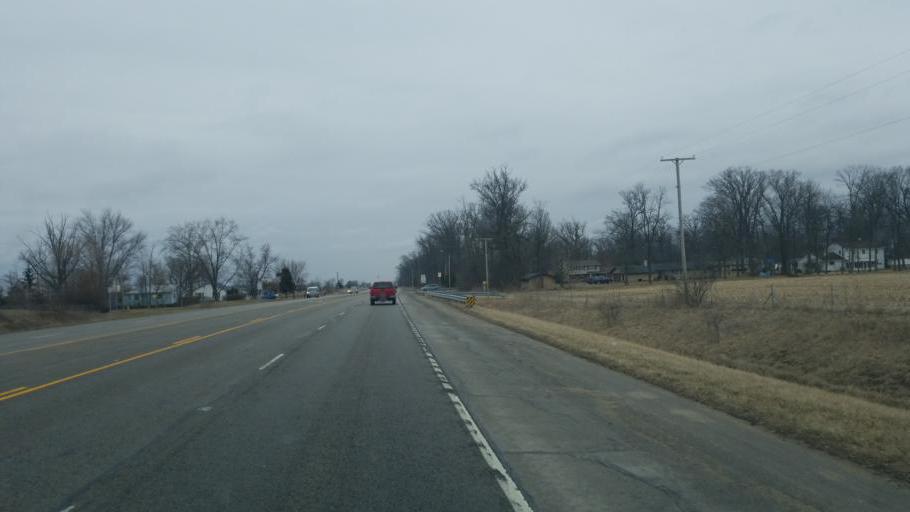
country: US
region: Indiana
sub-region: Adams County
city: Decatur
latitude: 40.8007
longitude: -84.9373
